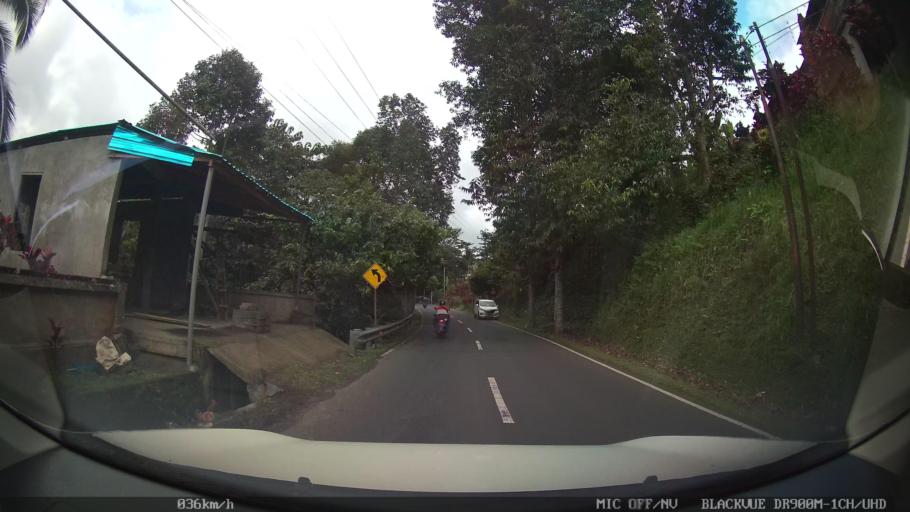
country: ID
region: Bali
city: Petang
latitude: -8.3823
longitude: 115.2208
